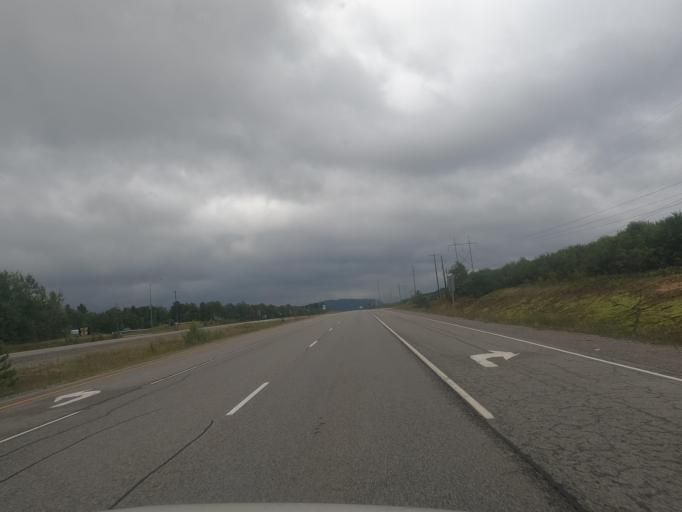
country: CA
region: Ontario
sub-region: Algoma
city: Sault Ste. Marie
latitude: 46.5577
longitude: -84.2129
